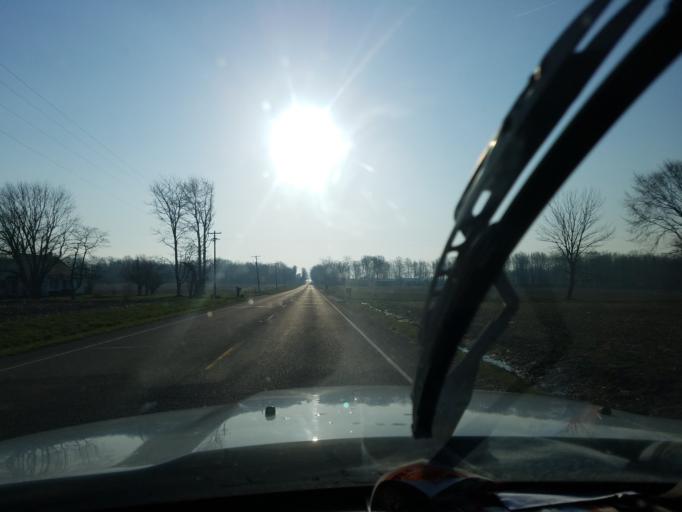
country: US
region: Indiana
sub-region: Vigo County
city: Seelyville
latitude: 39.3896
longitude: -87.2215
